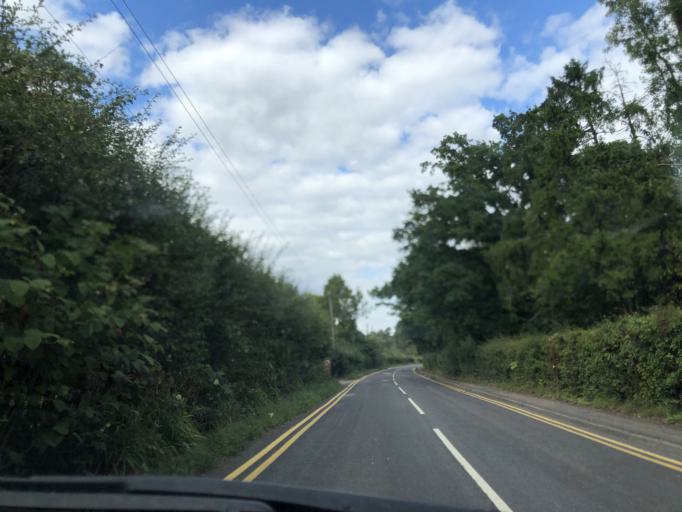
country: GB
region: England
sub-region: Kent
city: Tonbridge
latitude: 51.2183
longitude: 0.2271
